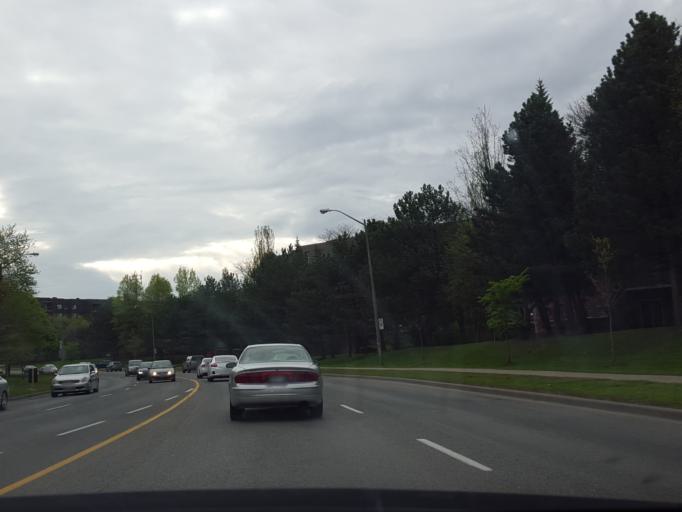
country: CA
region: Ontario
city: Willowdale
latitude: 43.7933
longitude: -79.3365
